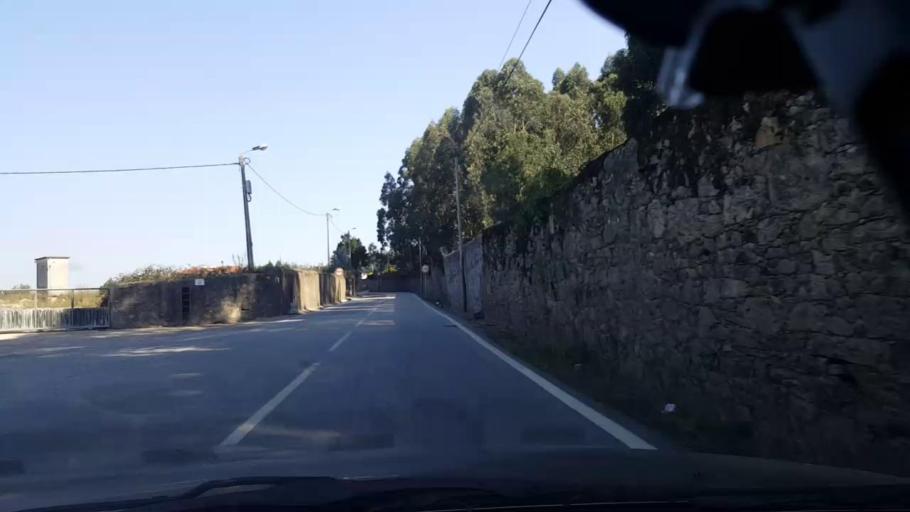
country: PT
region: Porto
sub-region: Vila do Conde
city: Arvore
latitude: 41.3666
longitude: -8.6694
